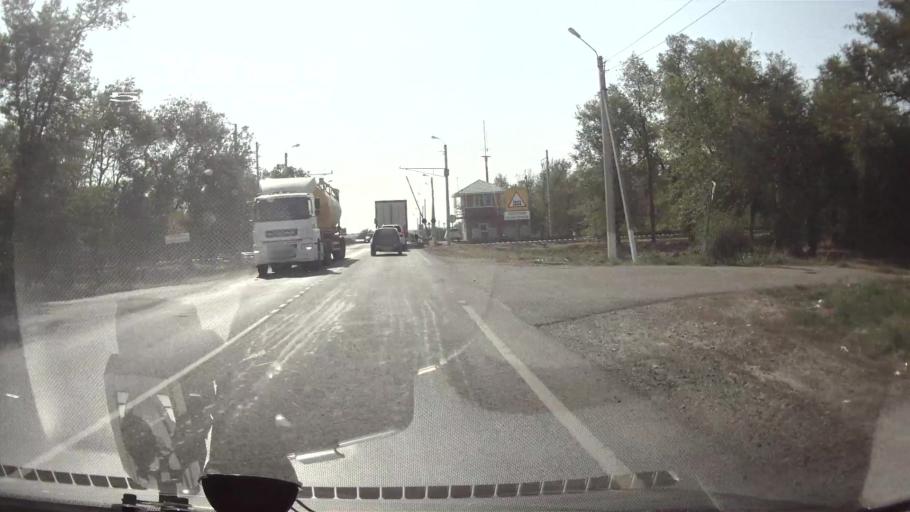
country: RU
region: Krasnodarskiy
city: Belaya Glina
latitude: 46.1005
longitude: 40.8538
